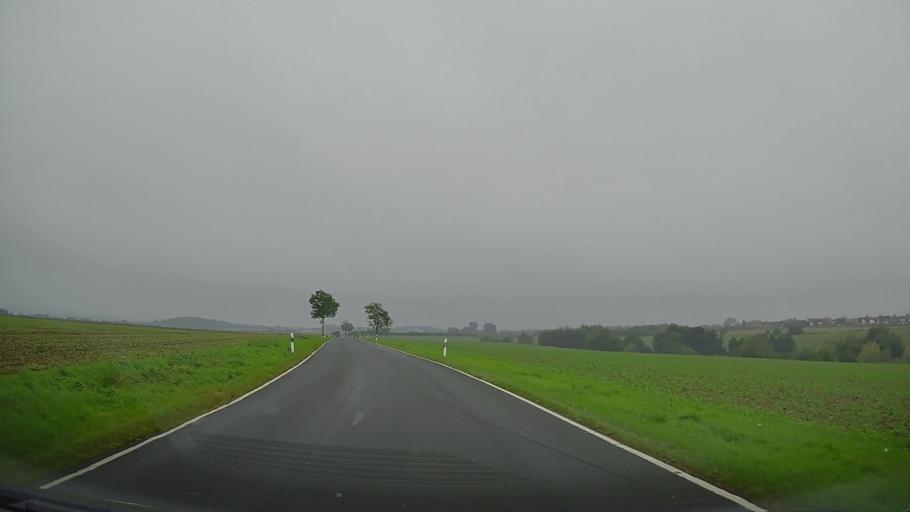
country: DE
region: Mecklenburg-Vorpommern
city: Wismar
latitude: 53.9146
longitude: 11.3959
